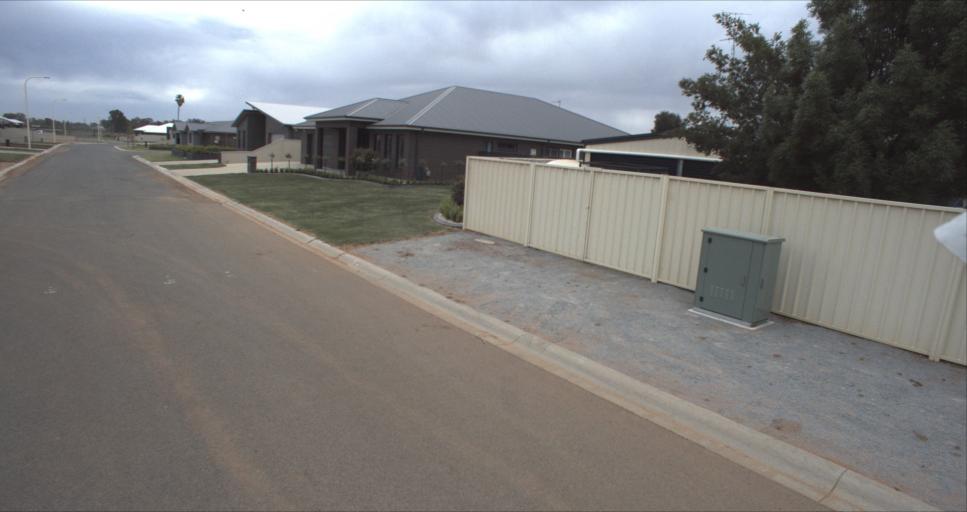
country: AU
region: New South Wales
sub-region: Leeton
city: Leeton
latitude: -34.5411
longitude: 146.4001
